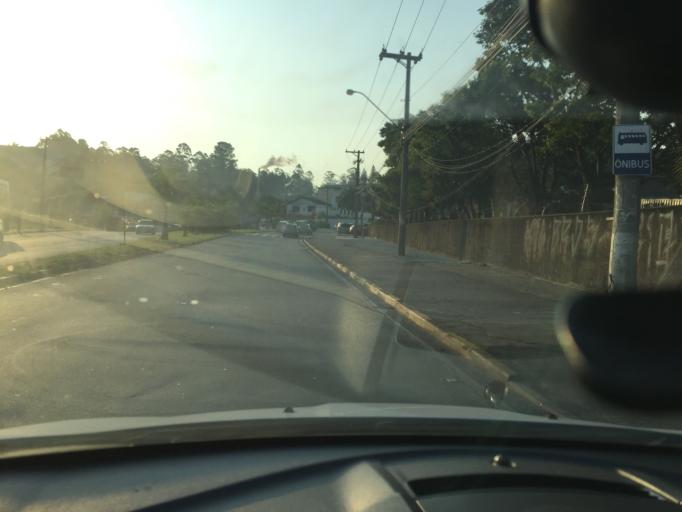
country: BR
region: Sao Paulo
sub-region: Varzea Paulista
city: Varzea Paulista
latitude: -23.2095
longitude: -46.8107
